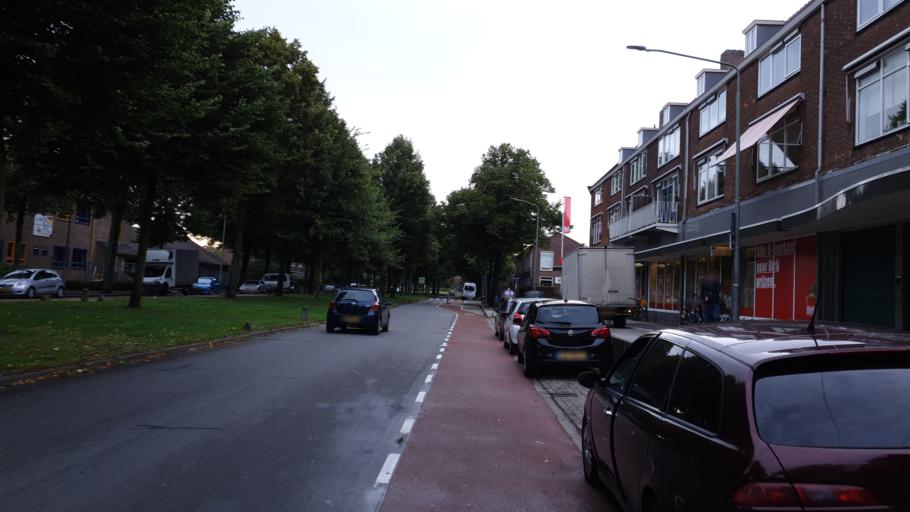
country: NL
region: South Holland
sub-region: Gemeente Dordrecht
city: Dordrecht
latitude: 51.8028
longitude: 4.6585
